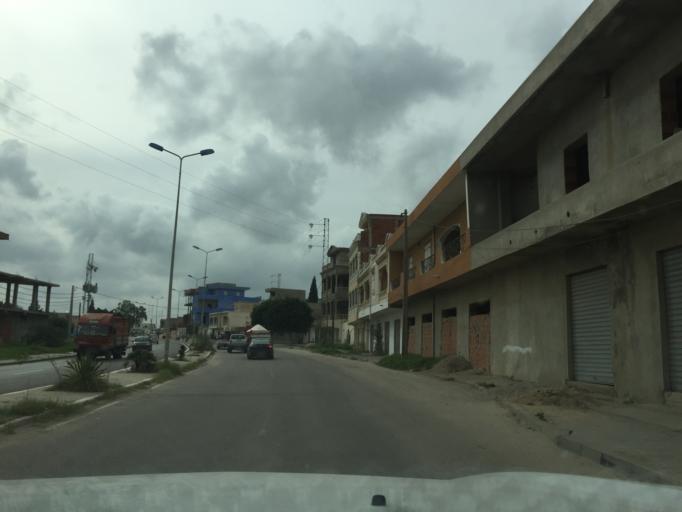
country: TN
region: Susah
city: Masakin
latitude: 35.6685
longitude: 10.5800
